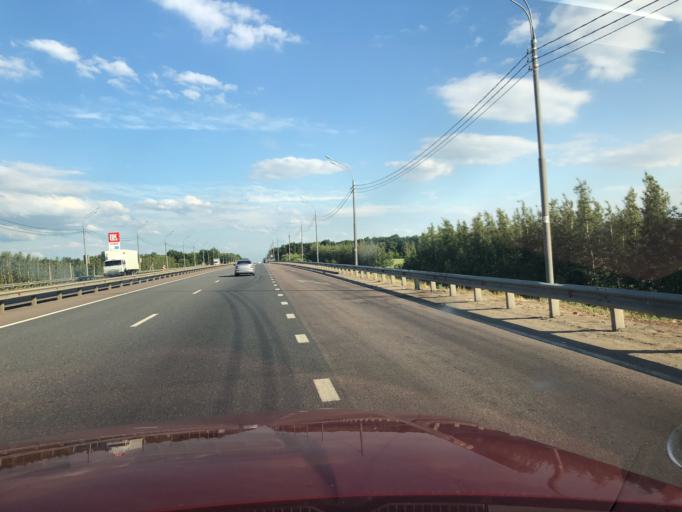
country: RU
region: Lipetsk
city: Zadonsk
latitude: 52.4256
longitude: 38.8300
